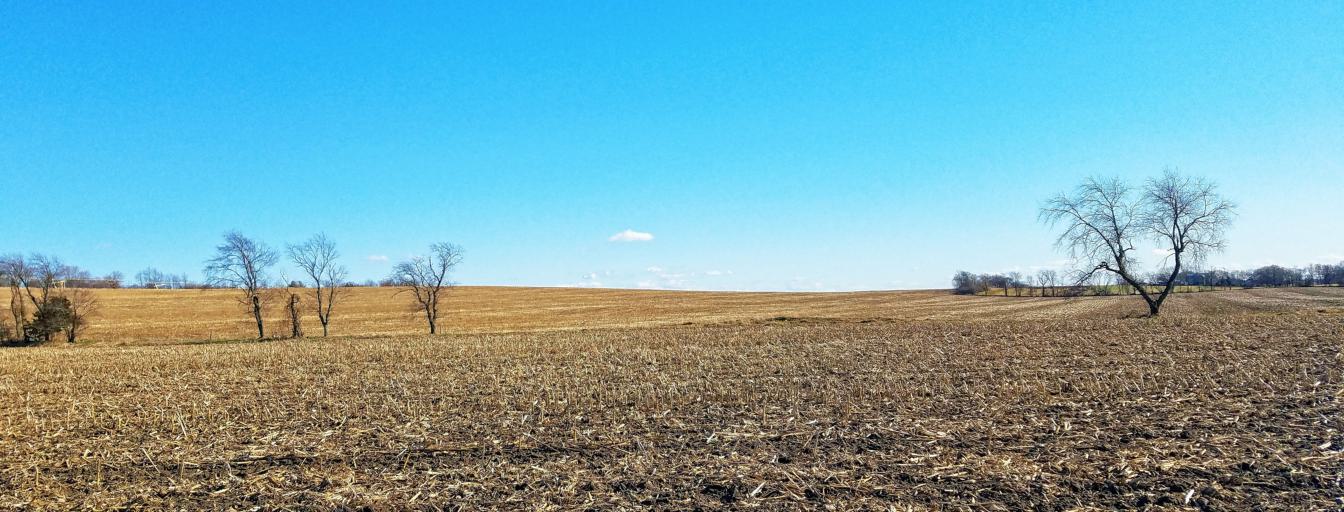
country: US
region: Wisconsin
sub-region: Jefferson County
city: Lake Mills
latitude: 43.0643
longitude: -88.9600
